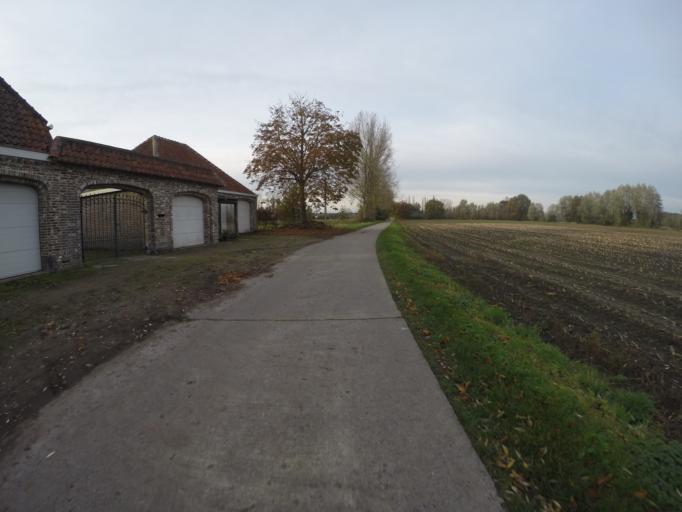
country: BE
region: Flanders
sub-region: Provincie Oost-Vlaanderen
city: Nevele
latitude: 51.0665
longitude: 3.5078
